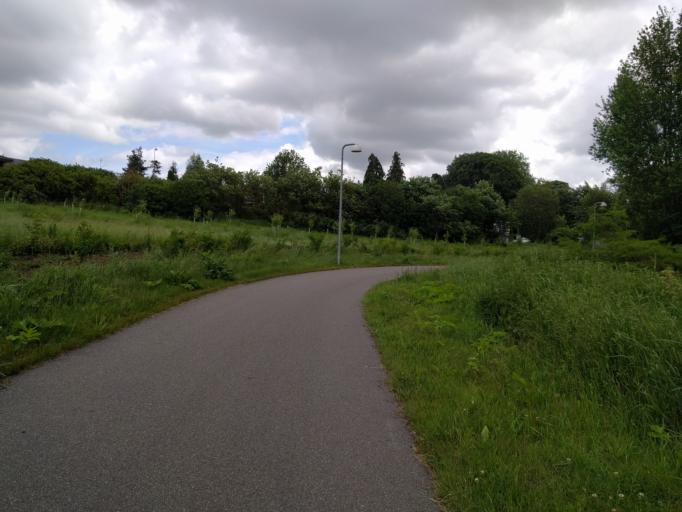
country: DK
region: South Denmark
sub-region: Odense Kommune
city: Bullerup
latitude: 55.4021
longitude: 10.4632
